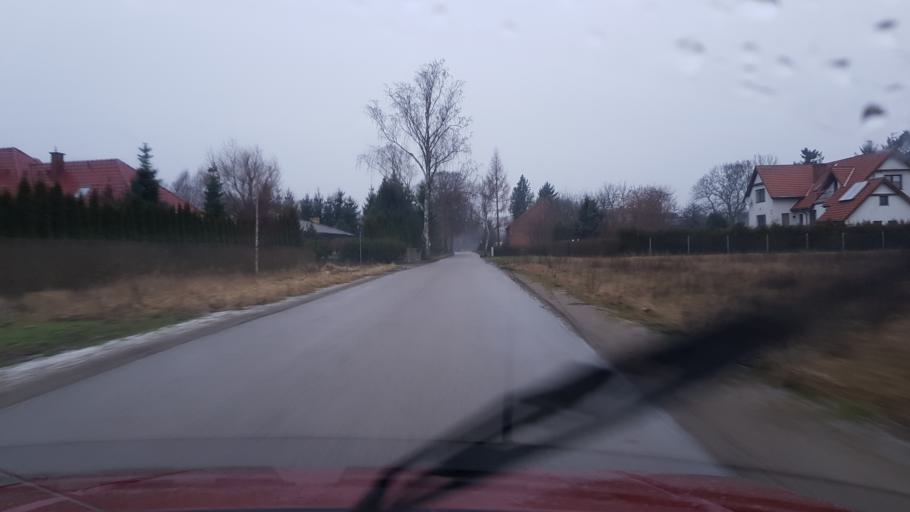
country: PL
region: West Pomeranian Voivodeship
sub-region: Koszalin
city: Koszalin
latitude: 54.1765
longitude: 16.2302
